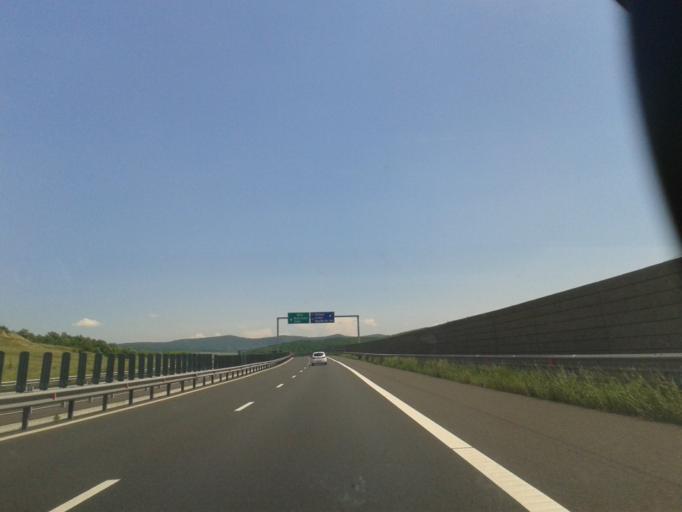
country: RO
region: Sibiu
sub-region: Comuna Apoldu de Jos
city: Apoldu de Jos
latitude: 45.8811
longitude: 23.8572
